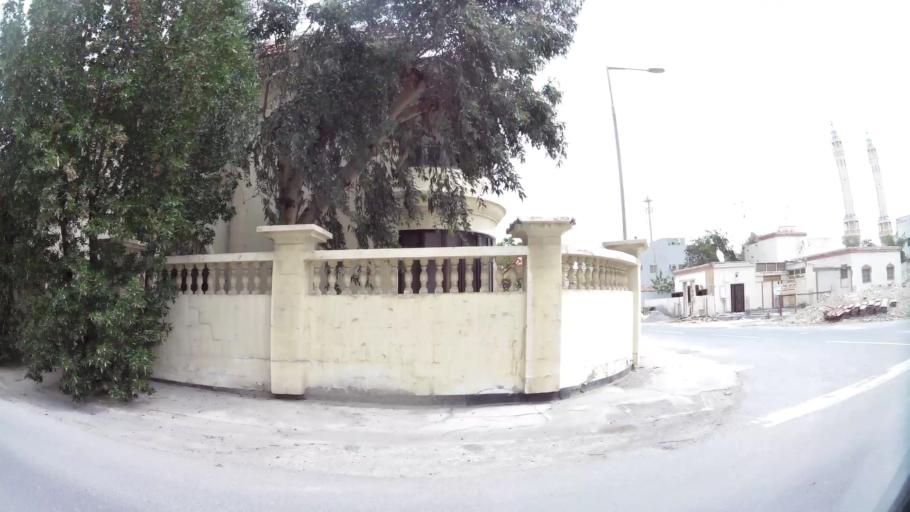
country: BH
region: Northern
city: Madinat `Isa
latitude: 26.1851
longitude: 50.5379
